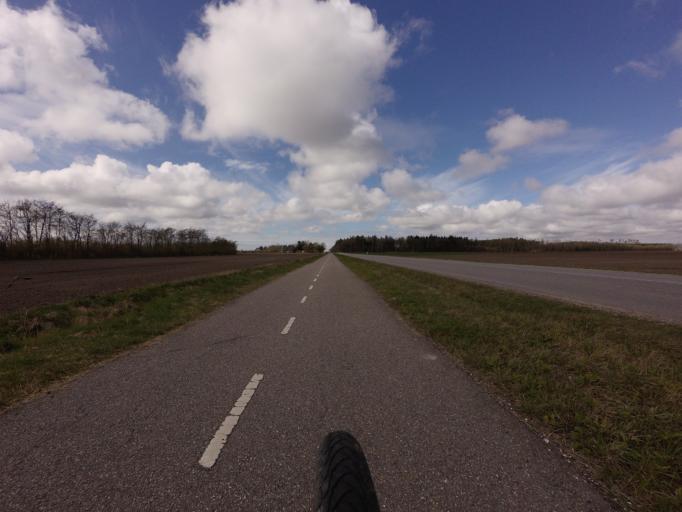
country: DK
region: North Denmark
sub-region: Hjorring Kommune
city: Vra
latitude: 57.3555
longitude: 9.8897
